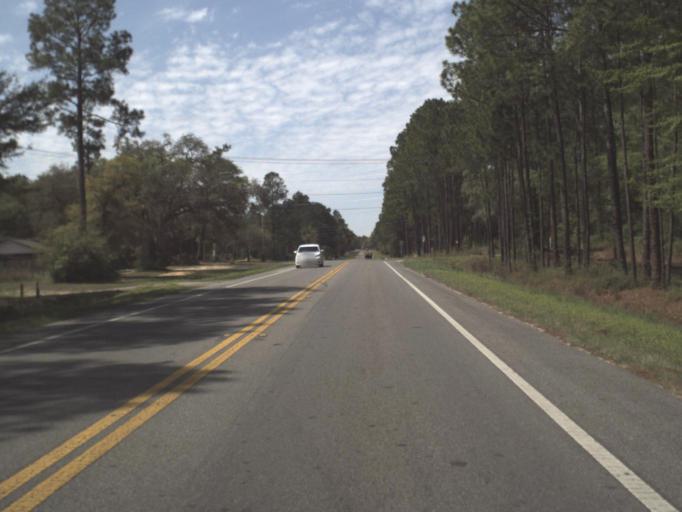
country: US
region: Florida
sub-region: Okaloosa County
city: Crestview
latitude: 30.7476
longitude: -86.6411
